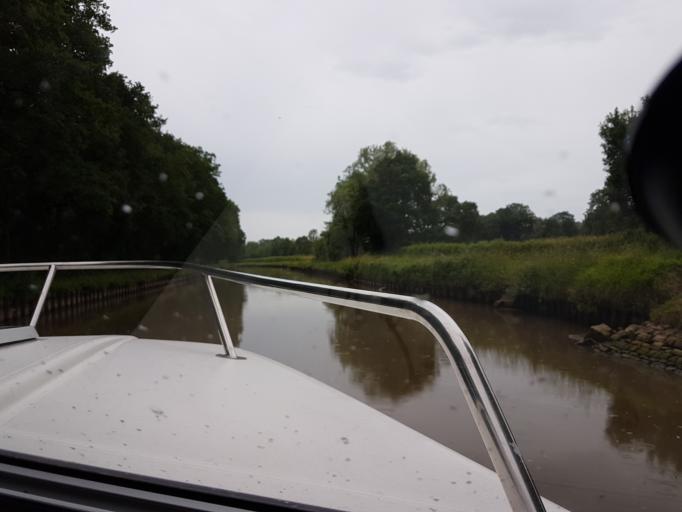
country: FR
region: Bourgogne
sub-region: Departement de la Nievre
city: Clamecy
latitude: 47.3686
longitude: 3.6108
